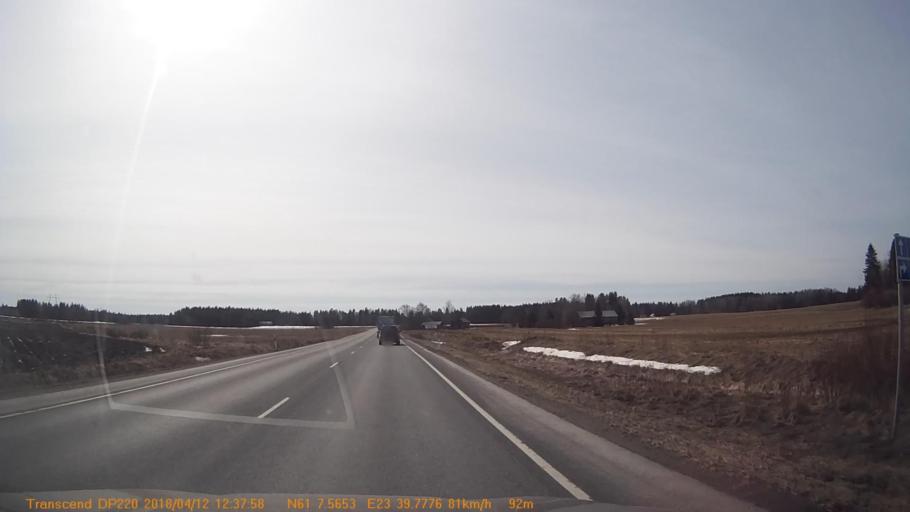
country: FI
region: Pirkanmaa
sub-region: Etelae-Pirkanmaa
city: Kylmaekoski
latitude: 61.1261
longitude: 23.6630
